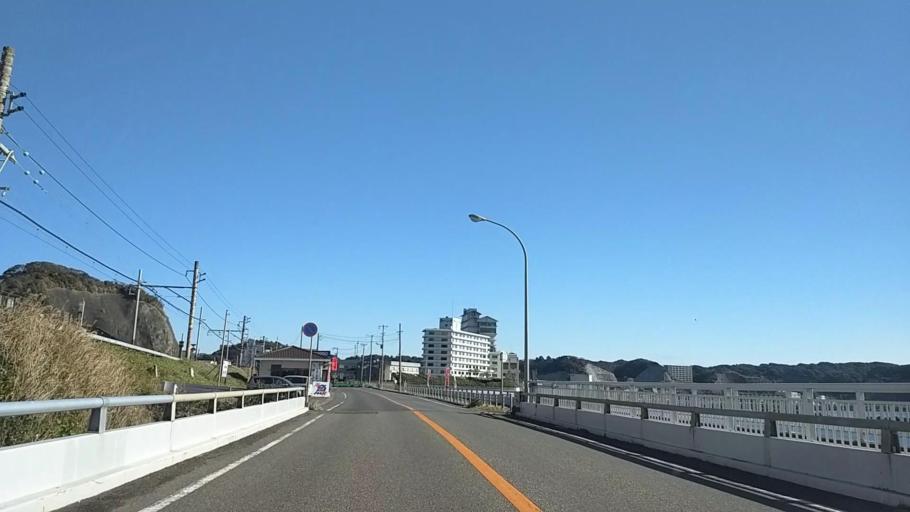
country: JP
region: Chiba
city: Katsuura
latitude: 35.1513
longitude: 140.3050
